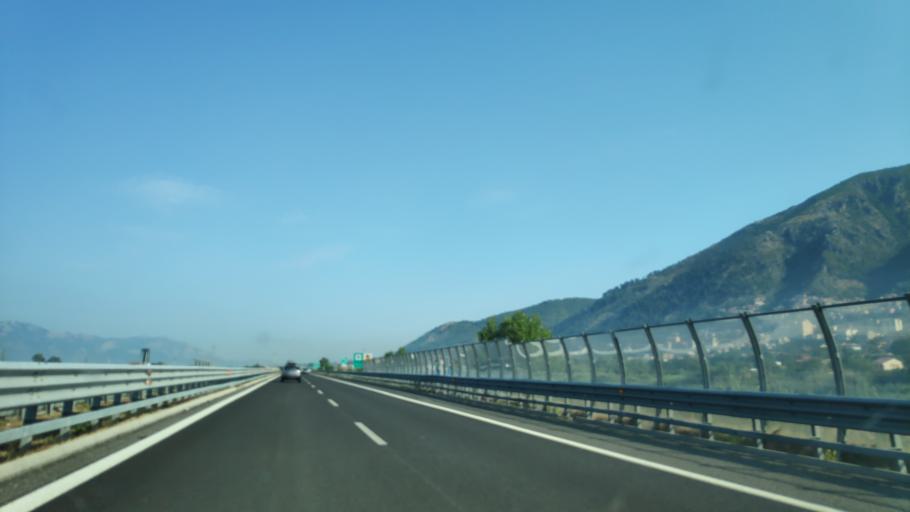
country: IT
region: Campania
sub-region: Provincia di Salerno
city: Sala Consilina
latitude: 40.3895
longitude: 15.5876
